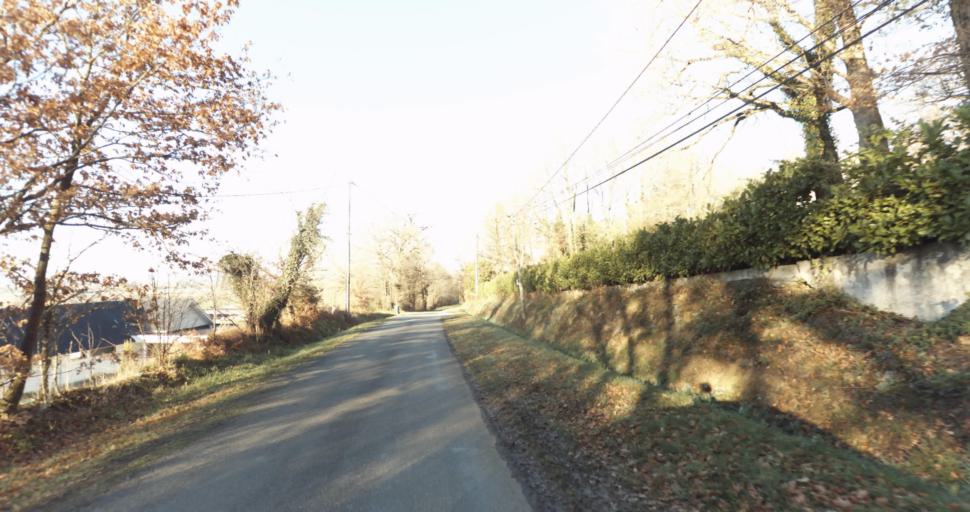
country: FR
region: Aquitaine
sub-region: Departement des Pyrenees-Atlantiques
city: Ousse
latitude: 43.3114
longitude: -0.2418
